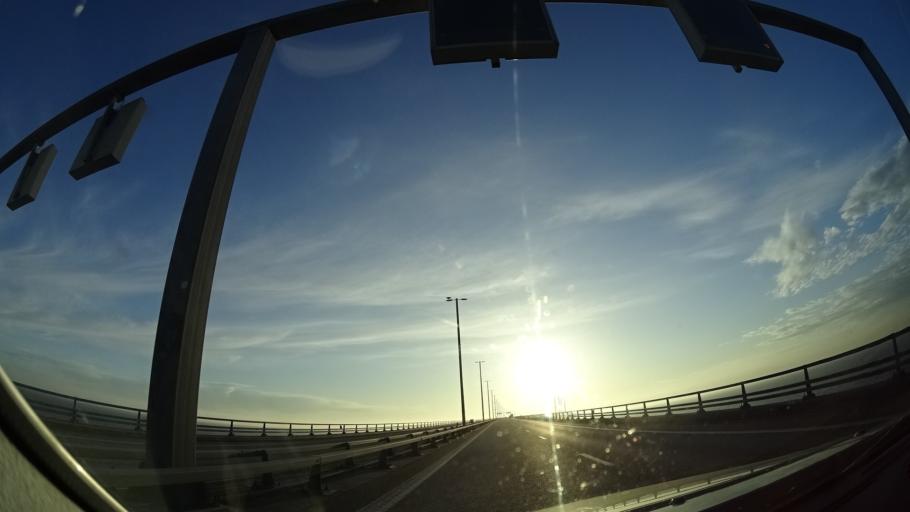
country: SE
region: Skane
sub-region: Malmo
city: Bunkeflostrand
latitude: 55.5661
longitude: 12.8843
